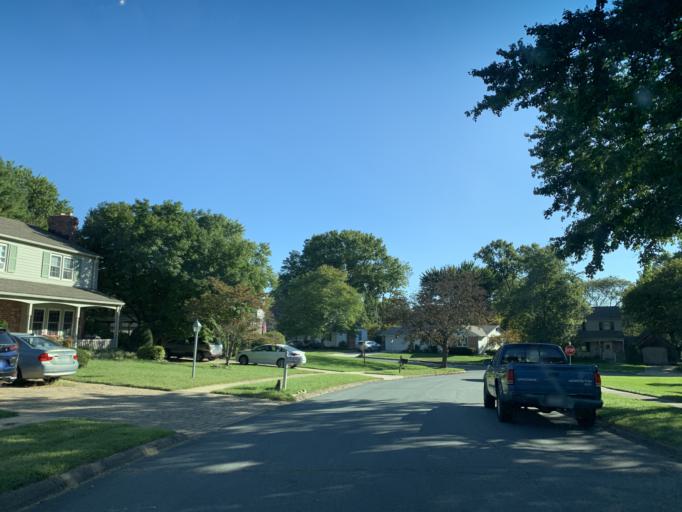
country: US
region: Maryland
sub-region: Harford County
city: Bel Air North
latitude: 39.5518
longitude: -76.3766
